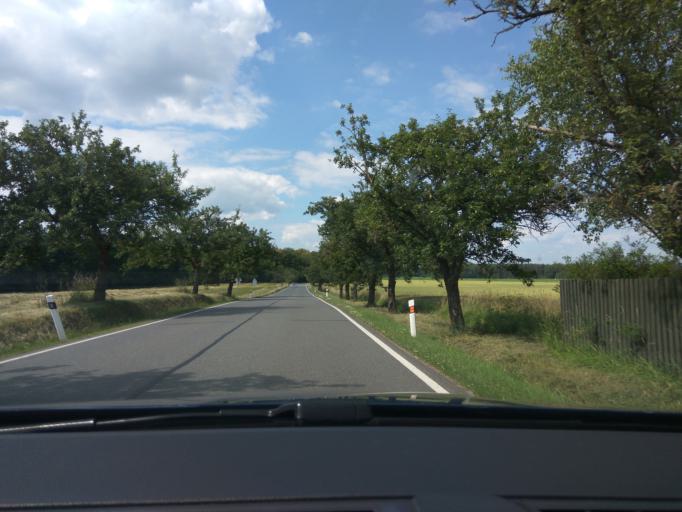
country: CZ
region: Jihocesky
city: Milevsko
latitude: 49.4141
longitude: 14.3585
